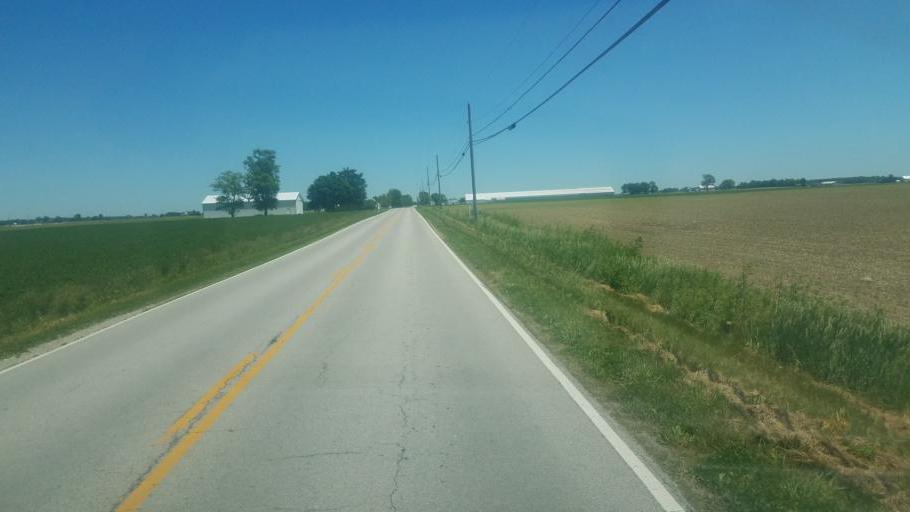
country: US
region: Ohio
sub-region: Darke County
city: Versailles
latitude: 40.2262
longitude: -84.4482
